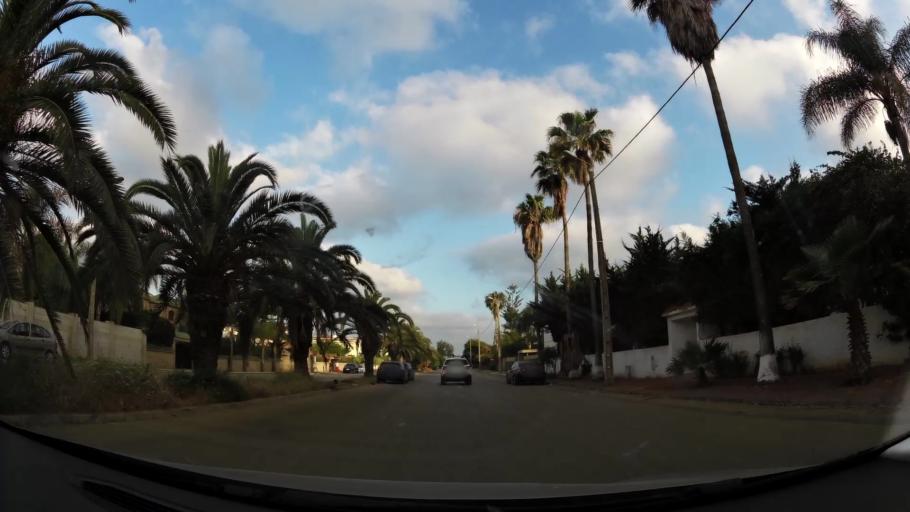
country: MA
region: Rabat-Sale-Zemmour-Zaer
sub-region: Rabat
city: Rabat
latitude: 33.9626
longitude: -6.8439
